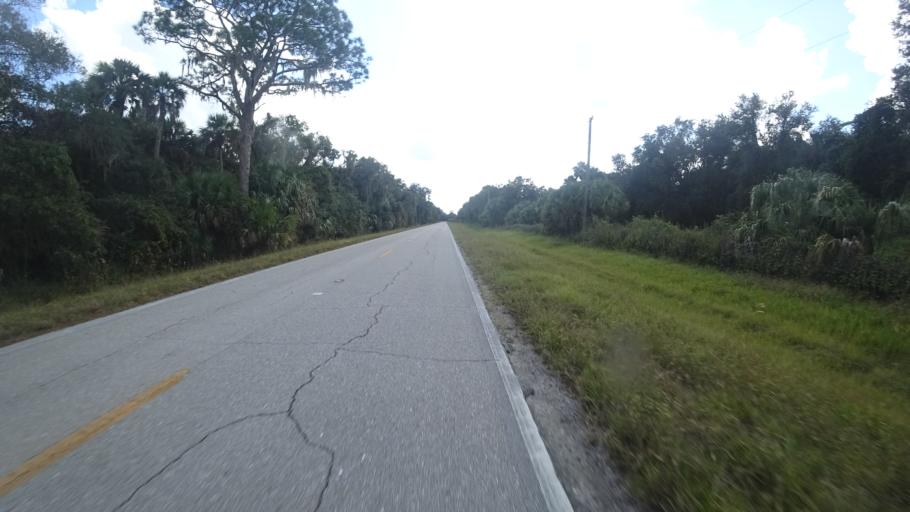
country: US
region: Florida
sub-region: Sarasota County
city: North Port
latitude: 27.2232
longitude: -82.1221
